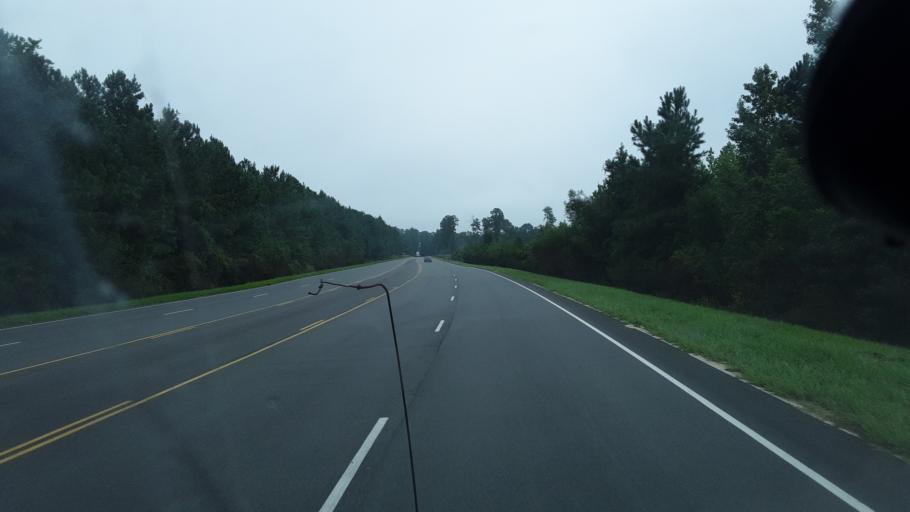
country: US
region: South Carolina
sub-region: Florence County
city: Johnsonville
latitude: 33.8861
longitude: -79.4494
